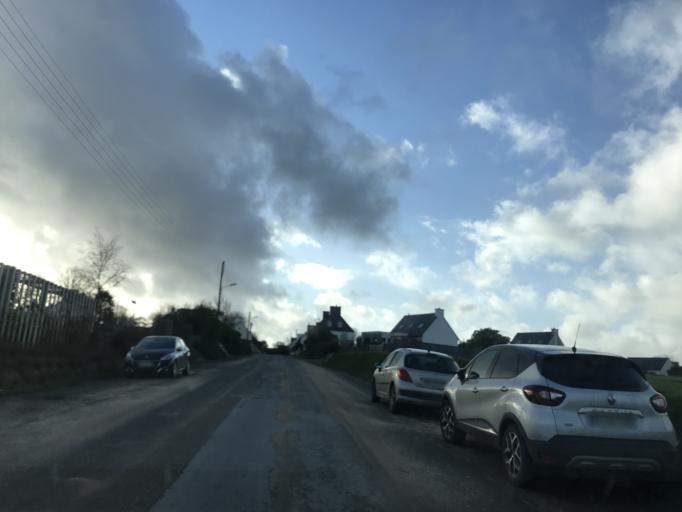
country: FR
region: Brittany
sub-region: Departement du Finistere
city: Lanmeur
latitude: 48.6478
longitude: -3.7090
